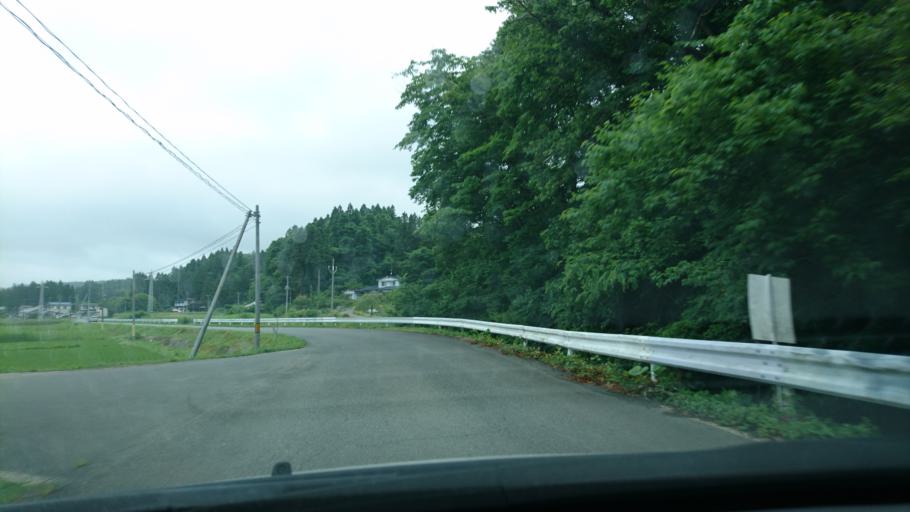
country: JP
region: Iwate
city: Ichinoseki
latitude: 38.9459
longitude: 141.0620
